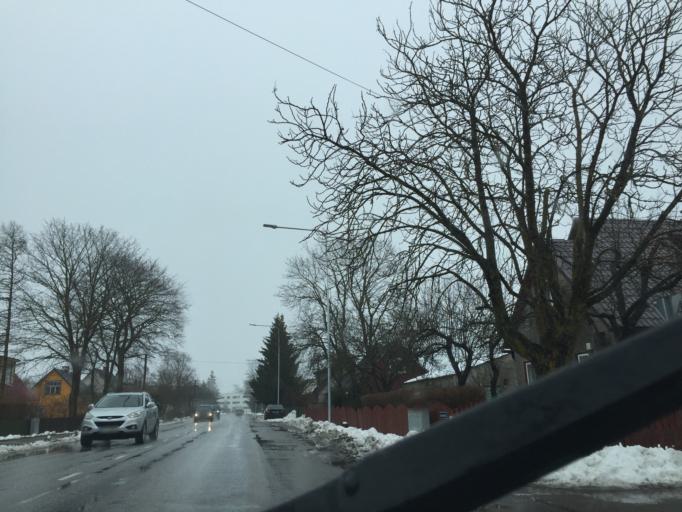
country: EE
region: Saare
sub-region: Kuressaare linn
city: Kuressaare
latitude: 58.2598
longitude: 22.4947
